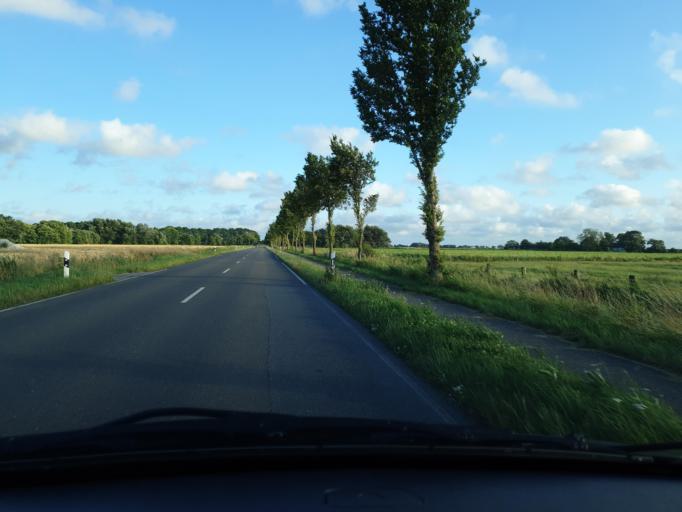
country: DE
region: Schleswig-Holstein
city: Wohrden
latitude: 54.1367
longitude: 9.0166
